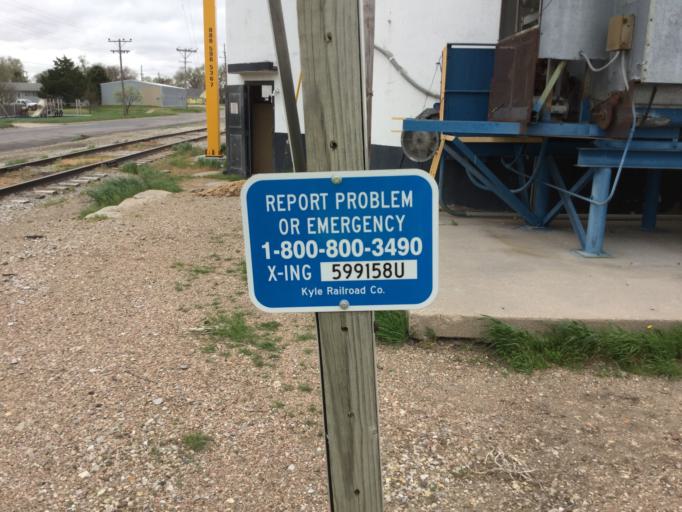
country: US
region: Kansas
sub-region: Phillips County
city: Phillipsburg
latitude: 39.7614
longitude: -99.3234
